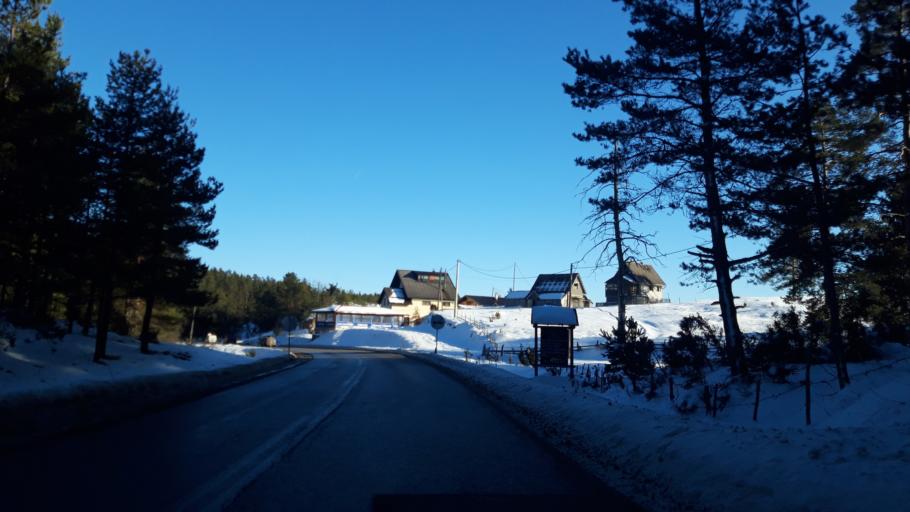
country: BA
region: Republika Srpska
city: Sokolac
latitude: 43.9185
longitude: 18.6950
